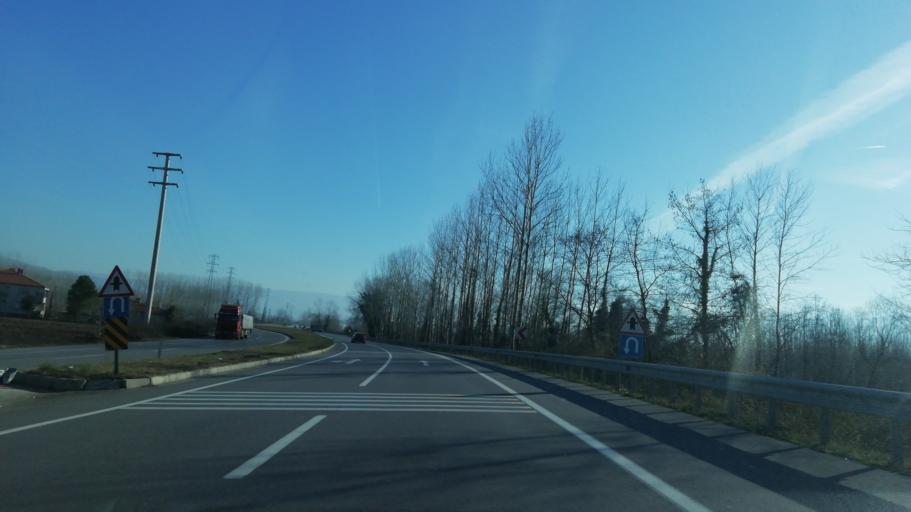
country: TR
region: Sakarya
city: Akyazi
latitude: 40.6985
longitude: 30.5682
